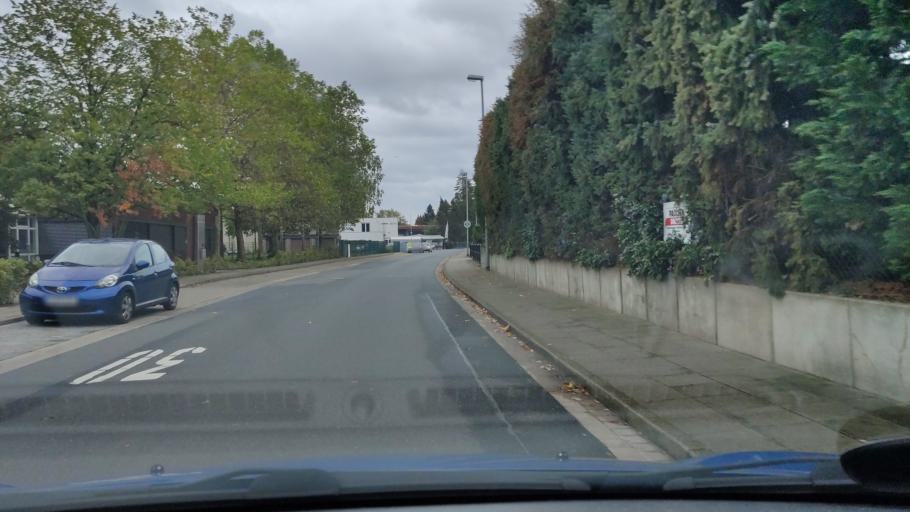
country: DE
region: Lower Saxony
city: Seelze
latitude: 52.3881
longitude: 9.6641
